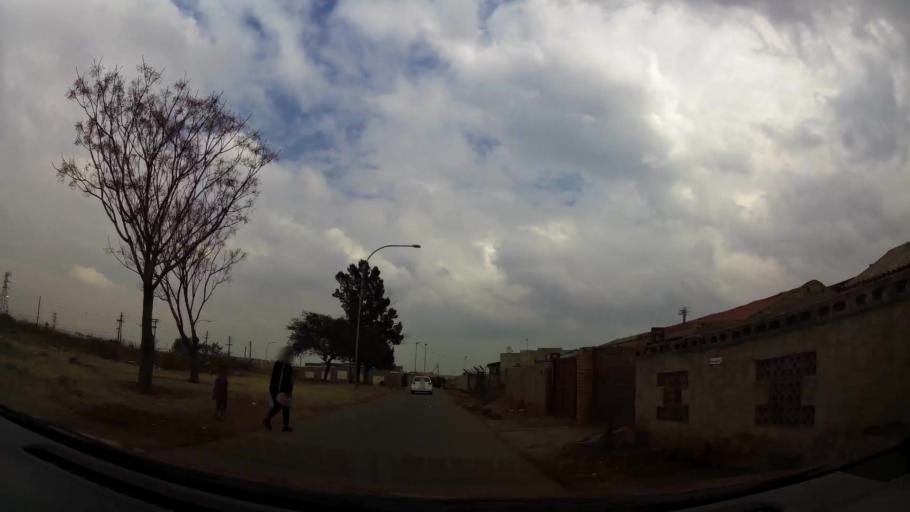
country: ZA
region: Gauteng
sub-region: City of Johannesburg Metropolitan Municipality
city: Soweto
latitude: -26.2578
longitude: 27.8263
